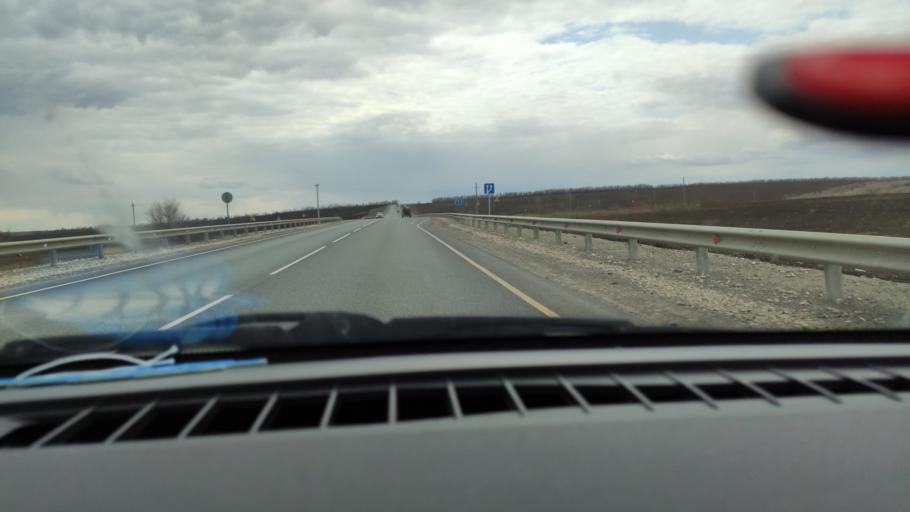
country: RU
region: Saratov
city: Yelshanka
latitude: 51.8405
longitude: 46.4775
